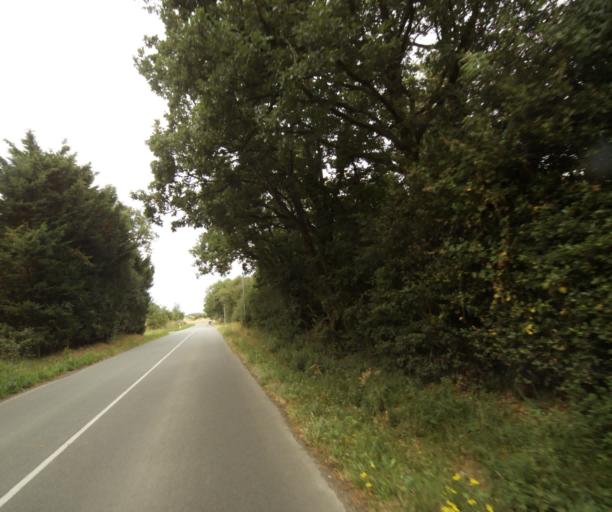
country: FR
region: Pays de la Loire
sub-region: Departement de la Vendee
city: Chateau-d'Olonne
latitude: 46.4917
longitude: -1.7045
